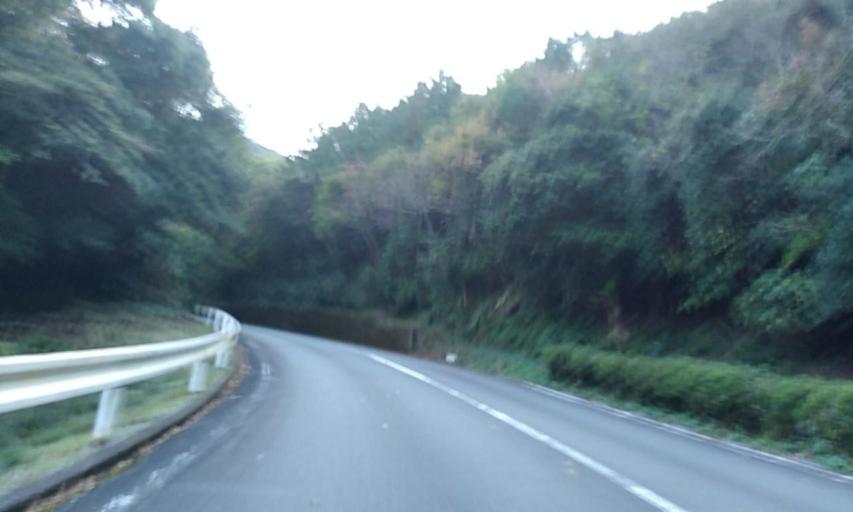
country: JP
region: Mie
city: Toba
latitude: 34.4825
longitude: 136.8348
